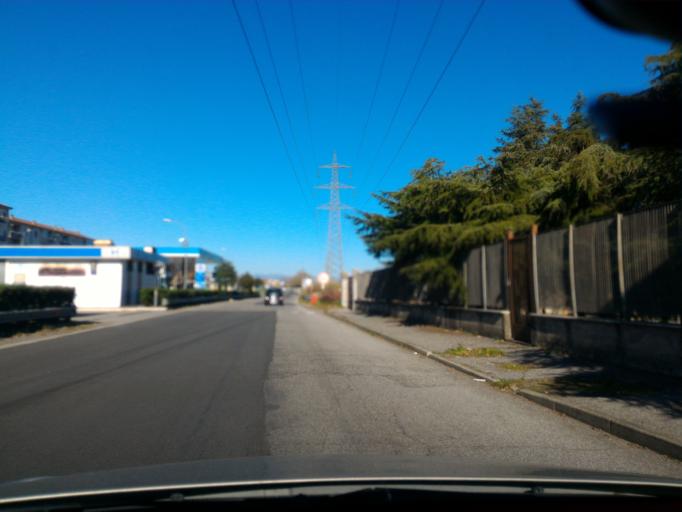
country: IT
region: Calabria
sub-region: Provincia di Cosenza
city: Cosenza
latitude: 39.3236
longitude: 16.2563
